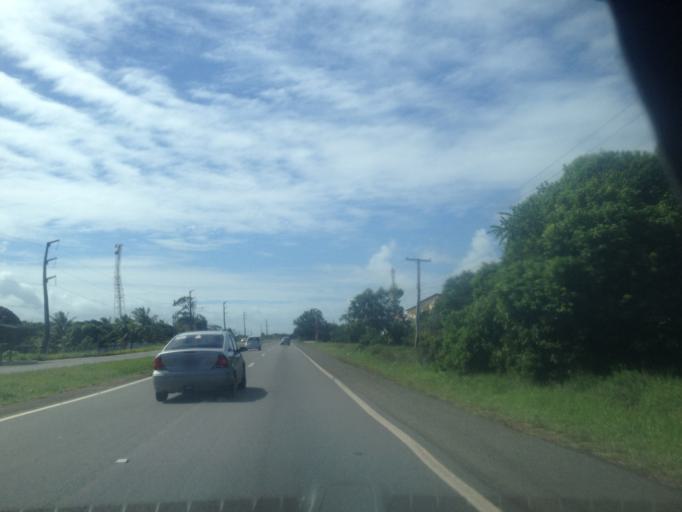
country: BR
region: Bahia
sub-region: Camacari
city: Camacari
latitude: -12.6537
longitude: -38.0854
